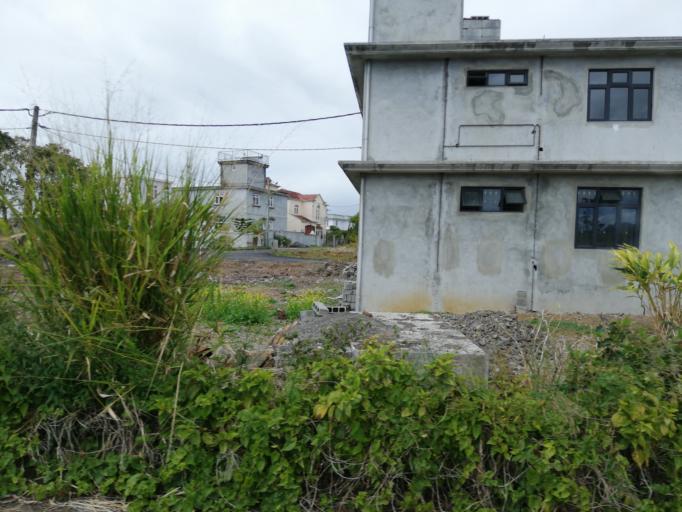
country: MU
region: Moka
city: Providence
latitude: -20.2468
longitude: 57.6085
